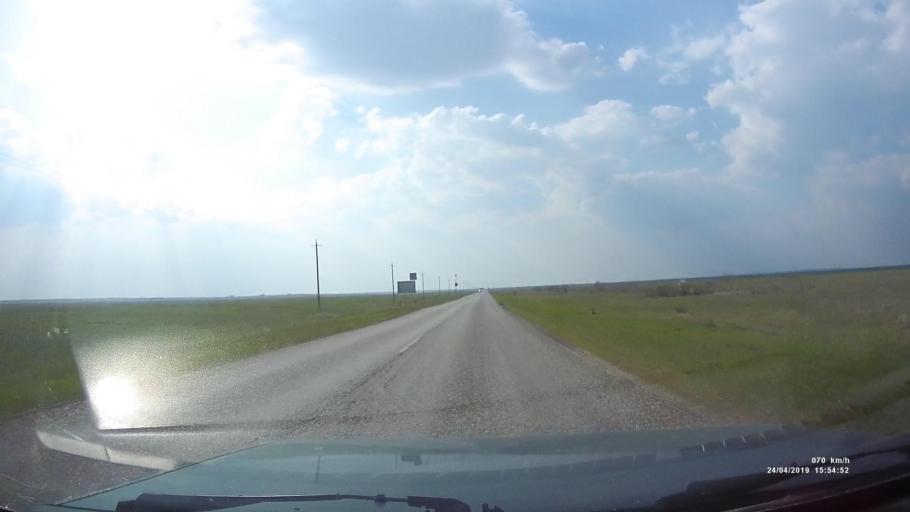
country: RU
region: Kalmykiya
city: Yashalta
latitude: 46.5868
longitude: 42.5597
